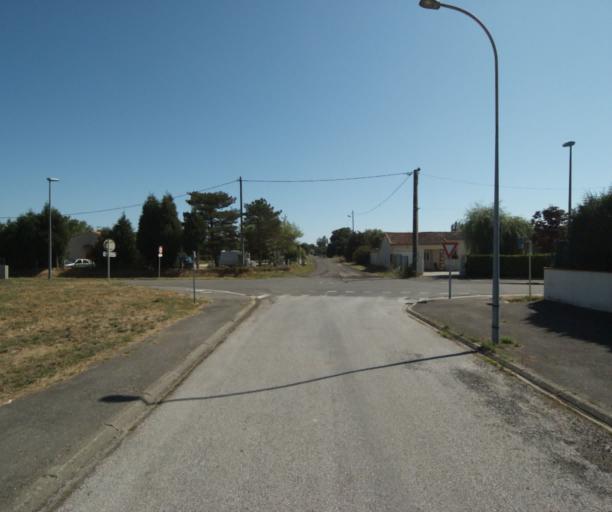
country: FR
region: Midi-Pyrenees
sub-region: Departement de la Haute-Garonne
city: Revel
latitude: 43.4649
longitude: 1.9954
